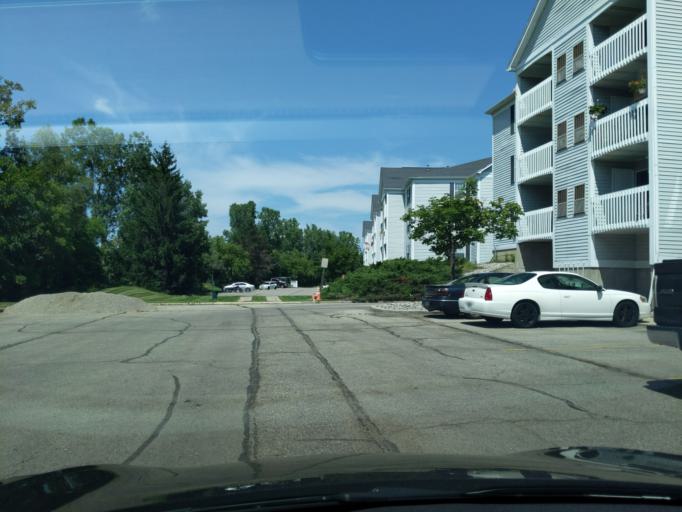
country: US
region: Michigan
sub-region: Eaton County
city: Waverly
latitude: 42.7434
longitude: -84.6488
